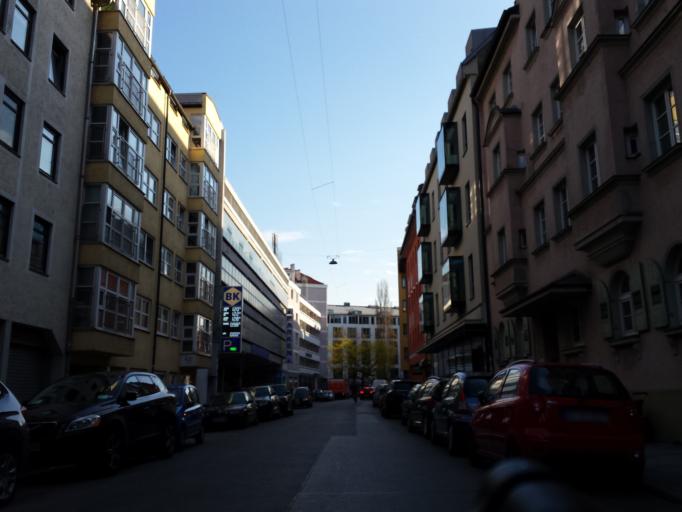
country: DE
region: Bavaria
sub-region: Upper Bavaria
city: Munich
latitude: 48.1327
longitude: 11.5806
